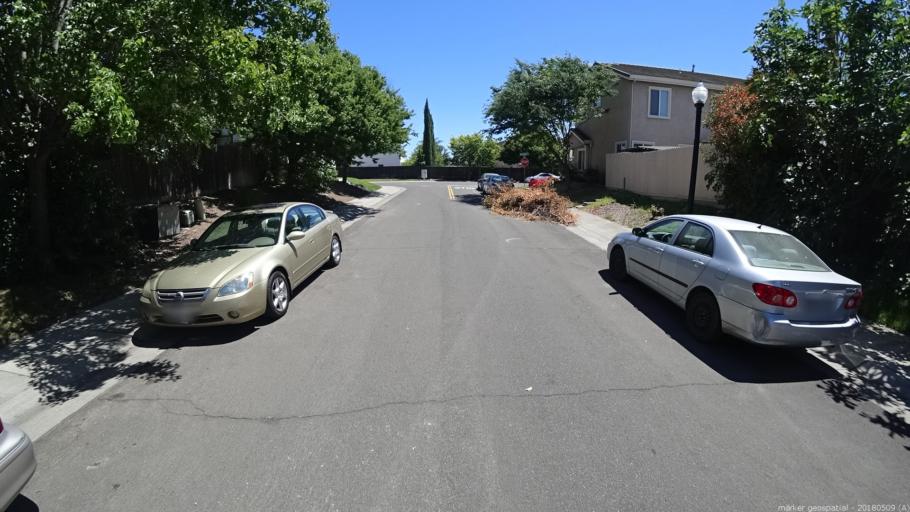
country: US
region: California
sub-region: Sacramento County
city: Sacramento
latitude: 38.6343
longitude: -121.5091
